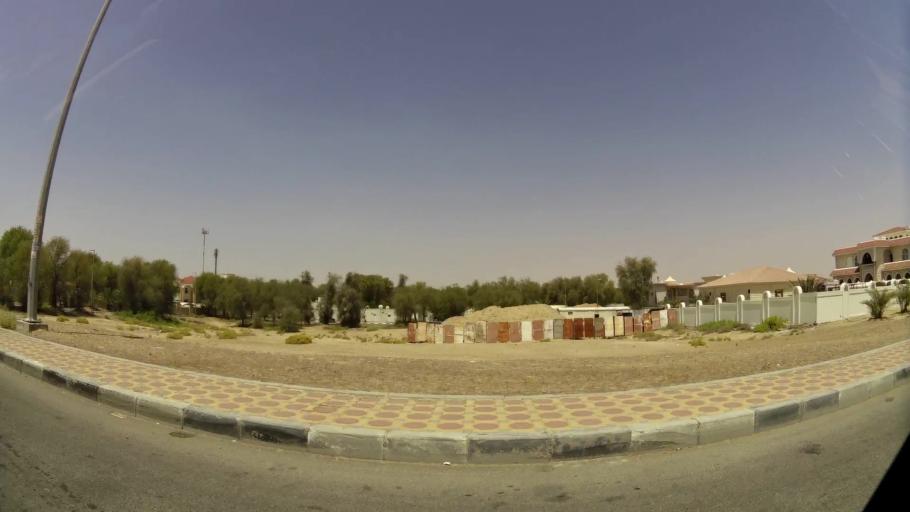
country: OM
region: Al Buraimi
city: Al Buraymi
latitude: 24.2769
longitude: 55.7479
